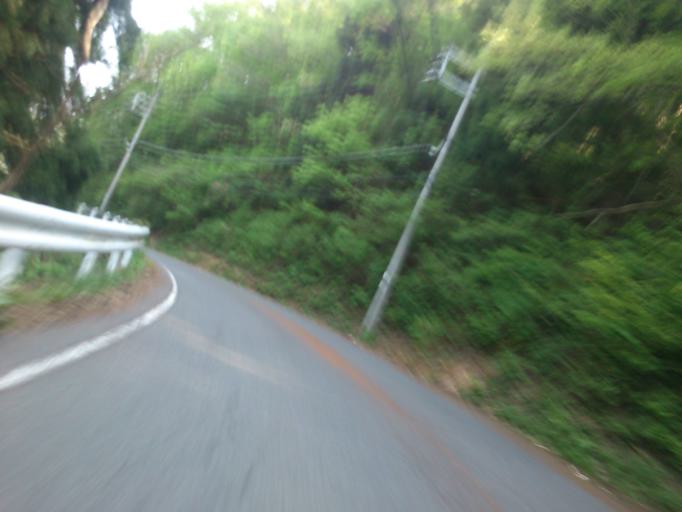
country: JP
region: Kyoto
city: Miyazu
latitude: 35.7132
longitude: 135.1930
